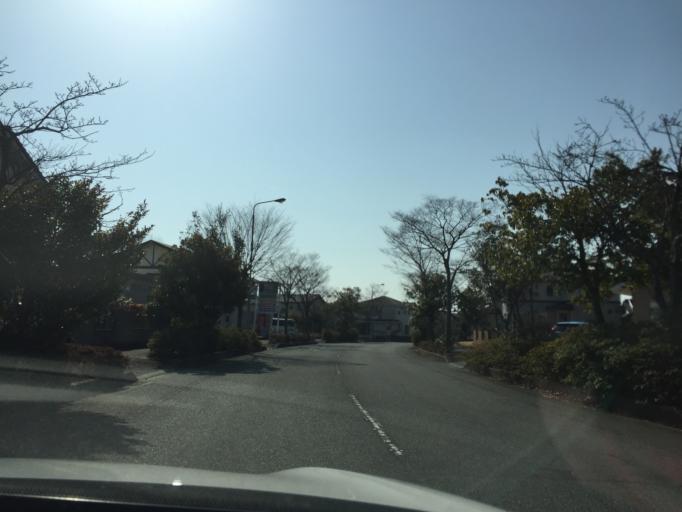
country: JP
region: Fukushima
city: Iwaki
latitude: 36.9686
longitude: 140.9351
